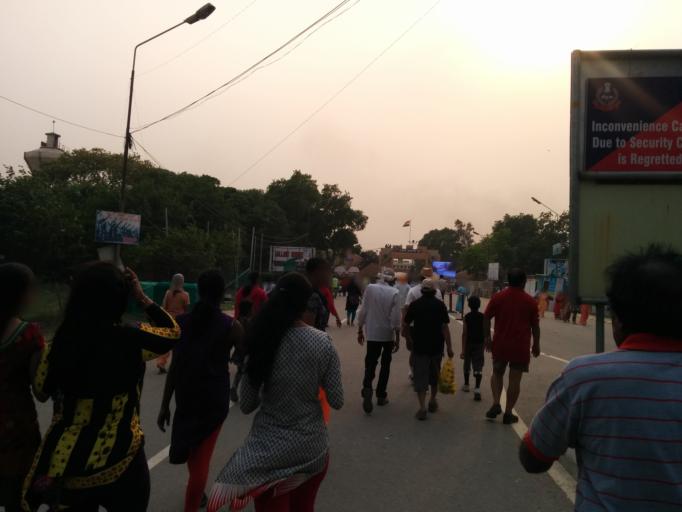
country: PK
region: Punjab
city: Lahore
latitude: 31.6049
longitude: 74.5755
